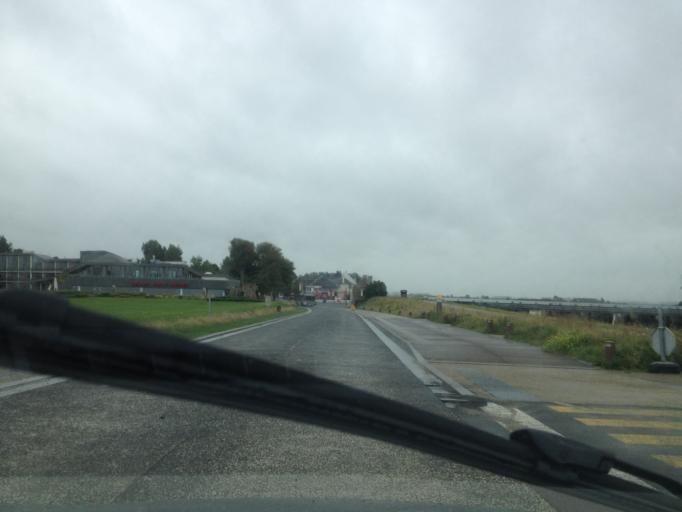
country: FR
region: Lower Normandy
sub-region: Departement de la Manche
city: Pontorson
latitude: 48.6191
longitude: -1.5109
